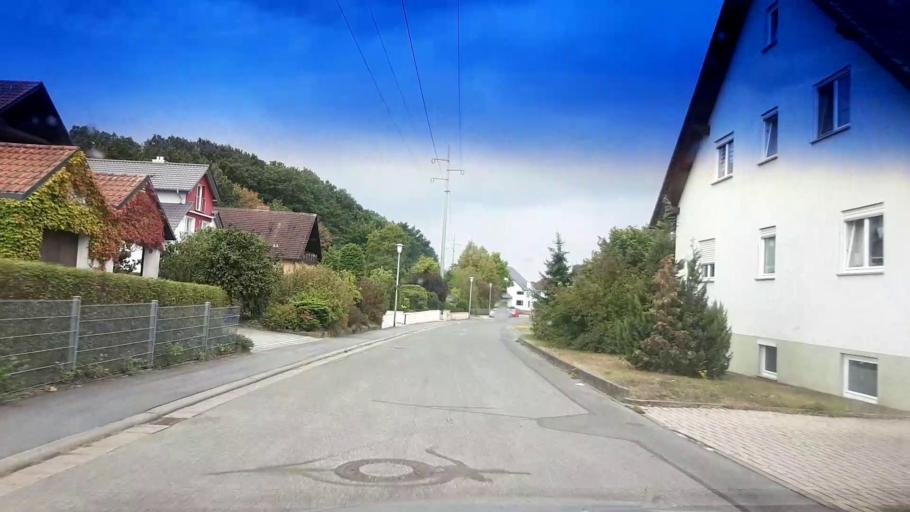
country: DE
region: Bavaria
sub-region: Upper Franconia
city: Breitengussbach
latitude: 49.9779
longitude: 10.9005
